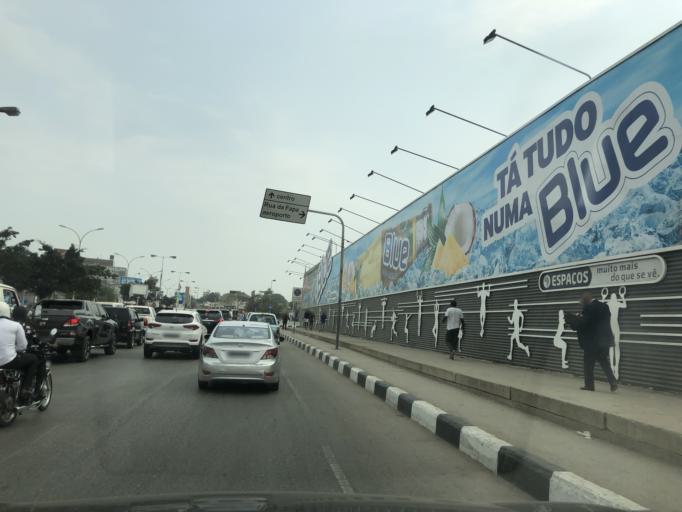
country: AO
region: Luanda
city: Luanda
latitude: -8.8481
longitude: 13.2116
